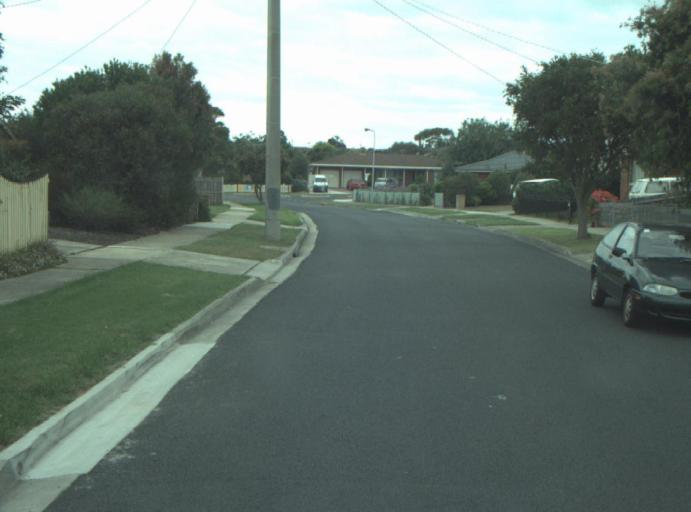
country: AU
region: Victoria
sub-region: Greater Geelong
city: Wandana Heights
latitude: -38.2027
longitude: 144.3244
